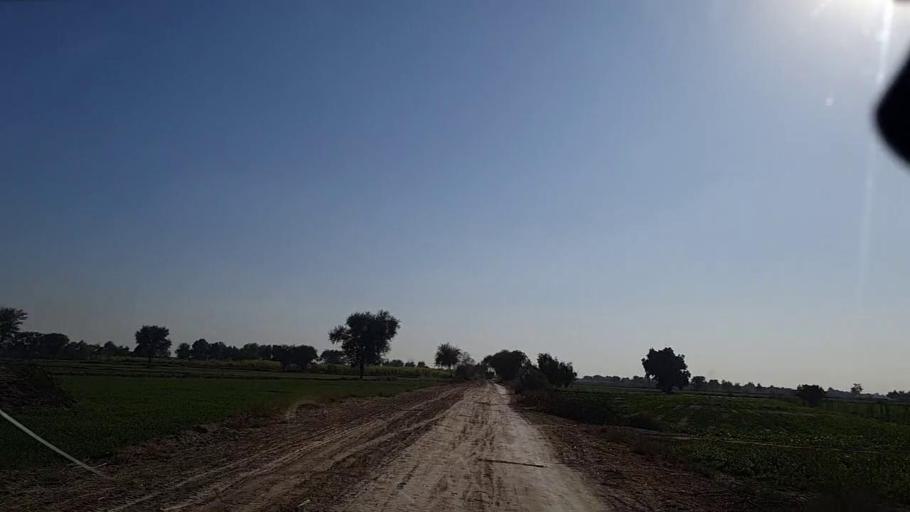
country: PK
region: Sindh
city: Khanpur
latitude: 27.7794
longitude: 69.3663
